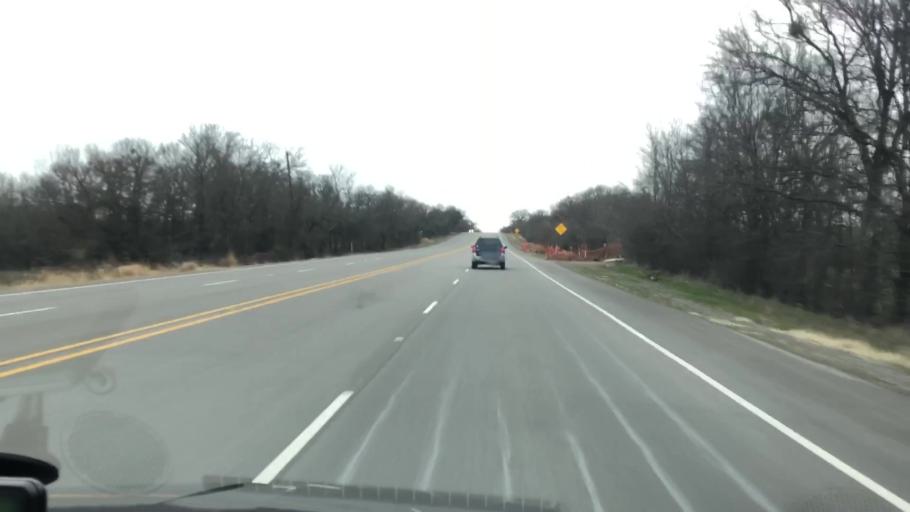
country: US
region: Texas
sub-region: Hamilton County
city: Hico
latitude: 32.0073
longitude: -98.0580
